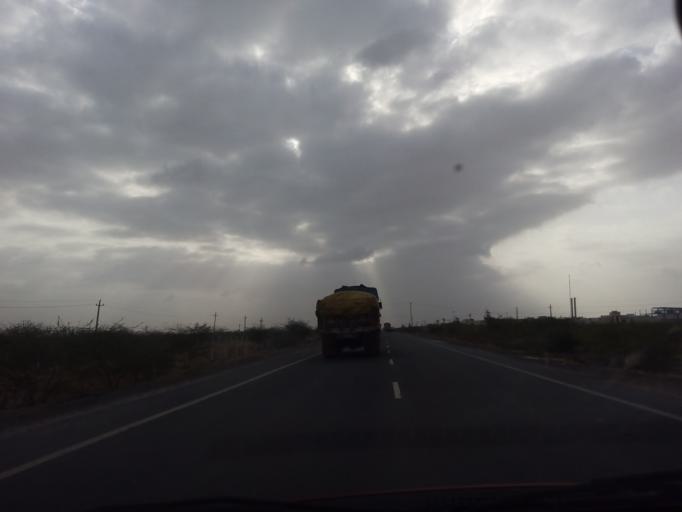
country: IN
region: Gujarat
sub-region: Kachchh
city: Bhuj
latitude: 23.2484
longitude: 69.8492
